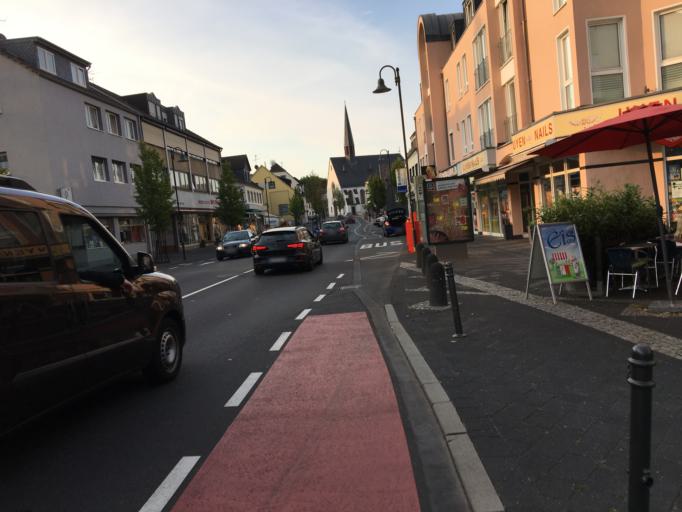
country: DE
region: North Rhine-Westphalia
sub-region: Regierungsbezirk Koln
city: Rosrath
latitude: 50.8959
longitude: 7.1823
